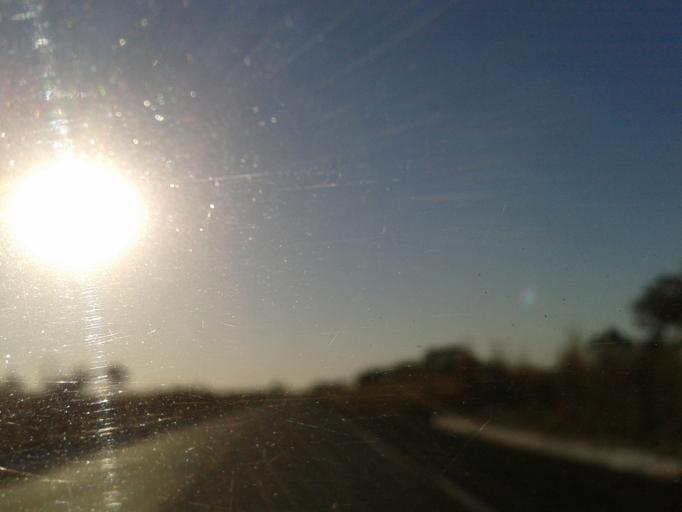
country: BR
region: Minas Gerais
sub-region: Santa Vitoria
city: Santa Vitoria
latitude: -19.0996
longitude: -50.3332
